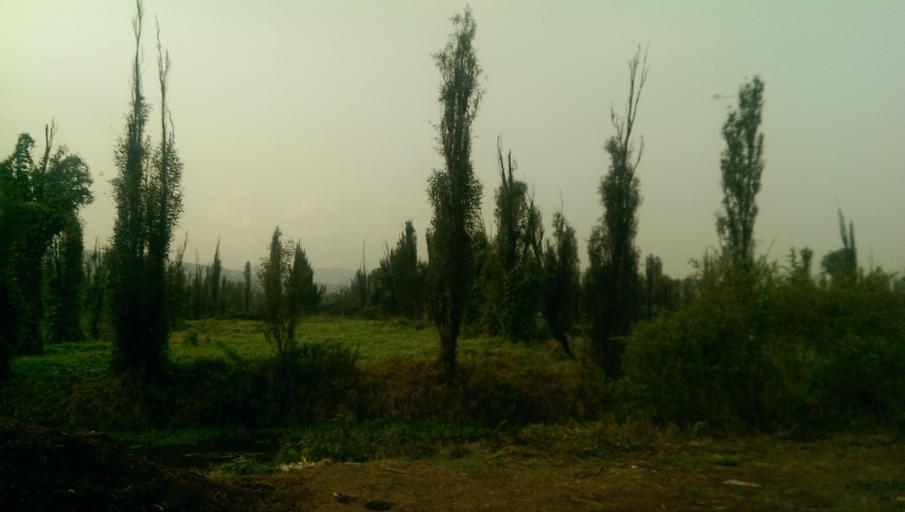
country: MX
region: Mexico City
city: Tlahuac
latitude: 19.2636
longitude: -99.0469
